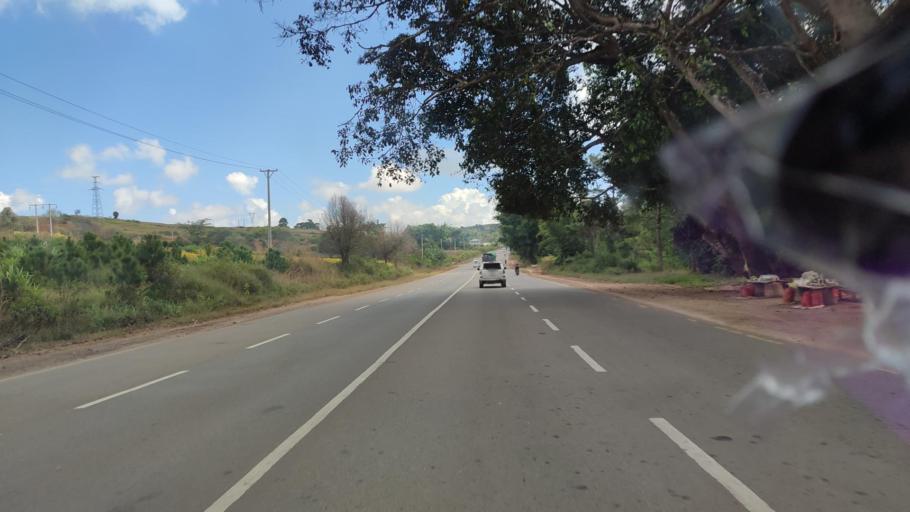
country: MM
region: Shan
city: Taunggyi
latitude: 20.6818
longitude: 96.7217
